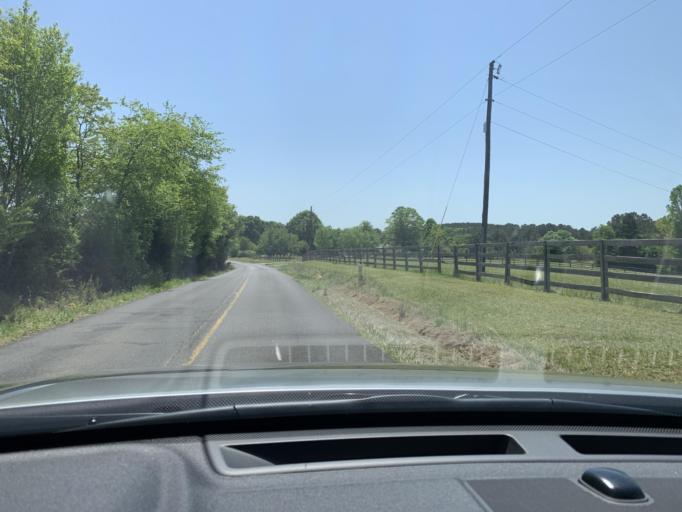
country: US
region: Georgia
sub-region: Polk County
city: Aragon
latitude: 34.0918
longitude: -85.1345
